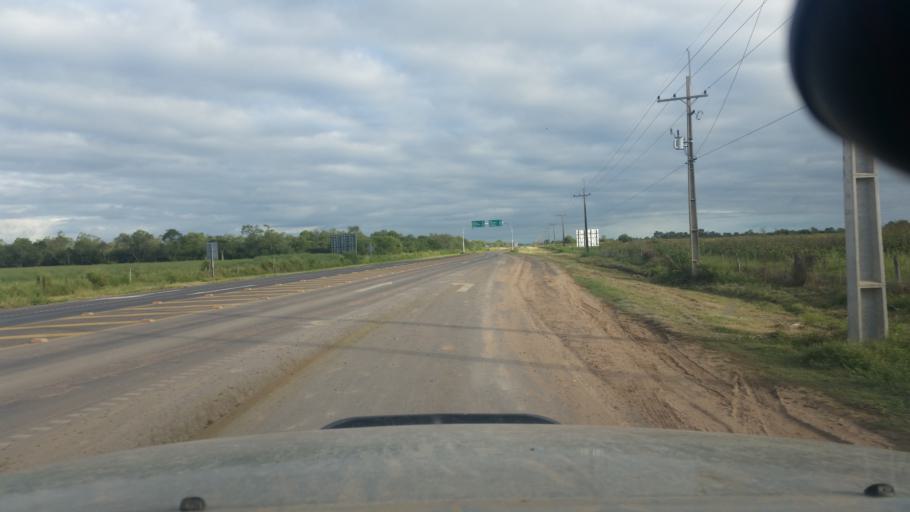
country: PY
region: Boqueron
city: Colonia Menno
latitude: -22.4674
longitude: -59.8383
